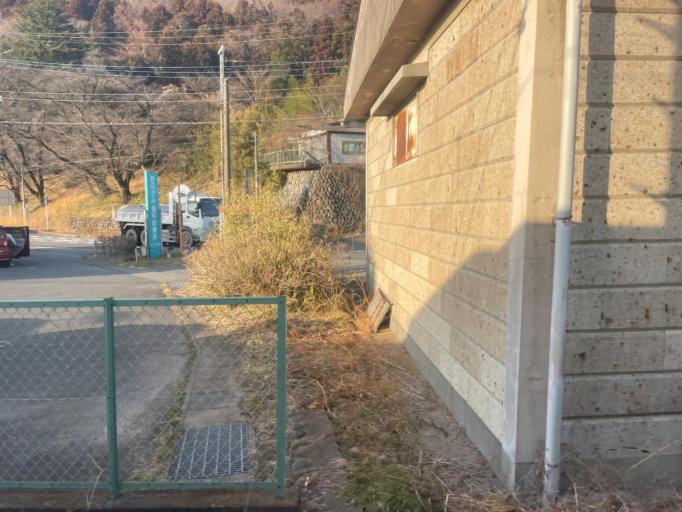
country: JP
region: Gunma
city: Shibukawa
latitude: 36.5487
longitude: 138.9357
